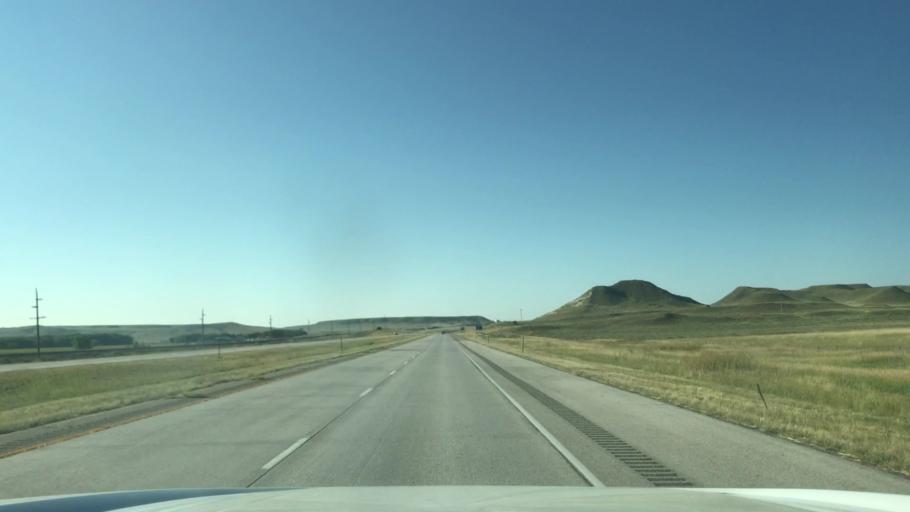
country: US
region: Wyoming
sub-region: Platte County
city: Guernsey
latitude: 42.5302
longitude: -105.0294
